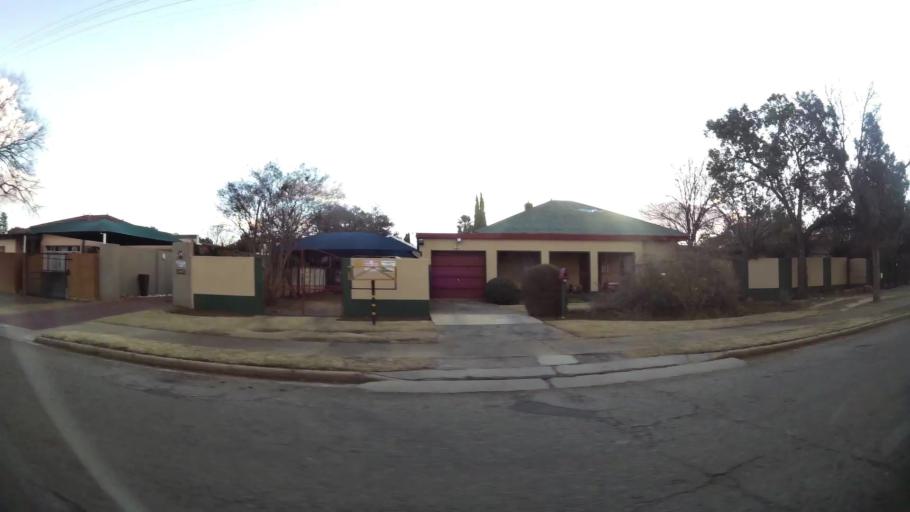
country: ZA
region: North-West
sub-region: Dr Kenneth Kaunda District Municipality
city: Potchefstroom
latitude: -26.7363
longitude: 27.0908
